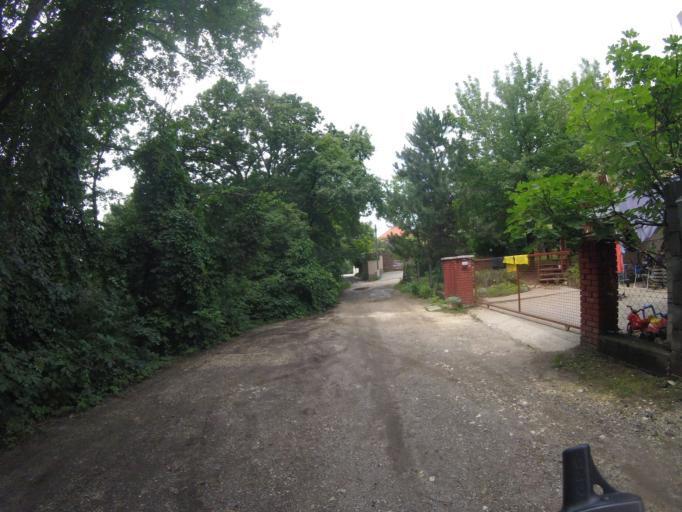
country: HU
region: Pest
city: Toeroekbalint
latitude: 47.4301
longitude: 18.9257
